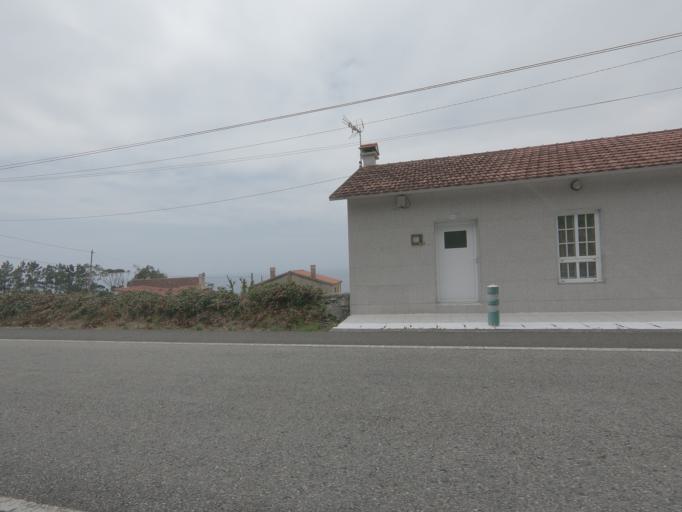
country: ES
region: Galicia
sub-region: Provincia de Pontevedra
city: Oia
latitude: 41.9965
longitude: -8.8770
